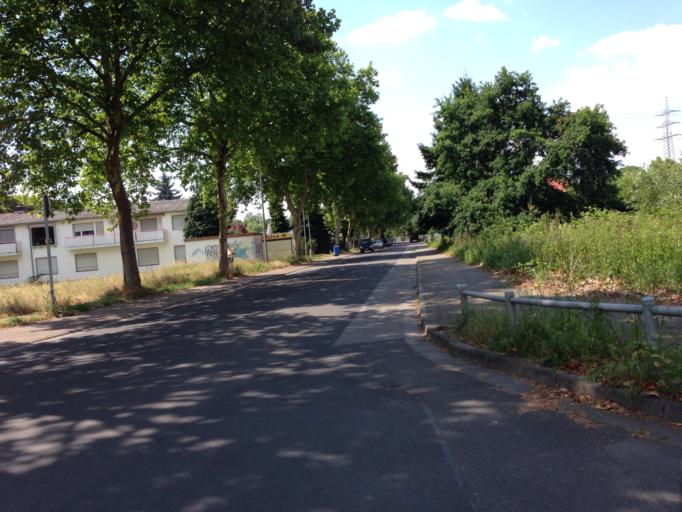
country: DE
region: Hesse
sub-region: Regierungsbezirk Darmstadt
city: Hanau am Main
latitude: 50.1089
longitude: 8.9300
